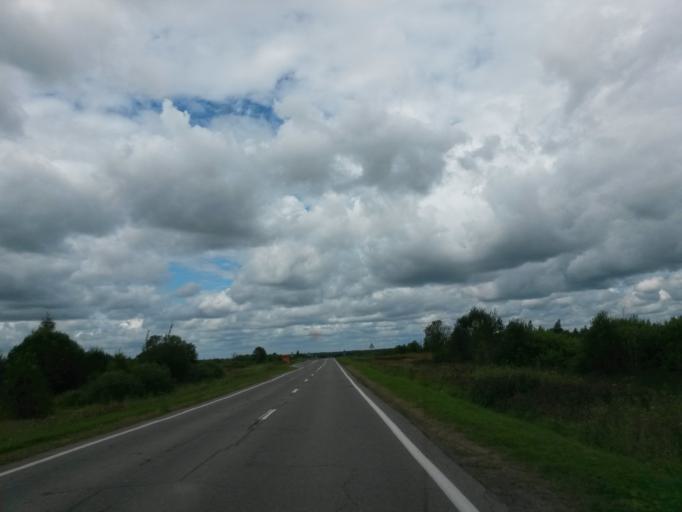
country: RU
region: Jaroslavl
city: Konstantinovskiy
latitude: 57.8681
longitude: 39.6020
